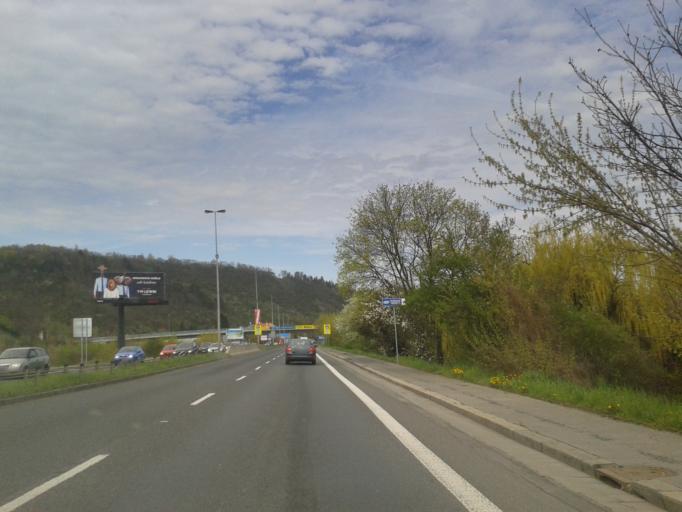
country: CZ
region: Praha
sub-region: Praha 12
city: Modrany
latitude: 50.0192
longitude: 14.3942
